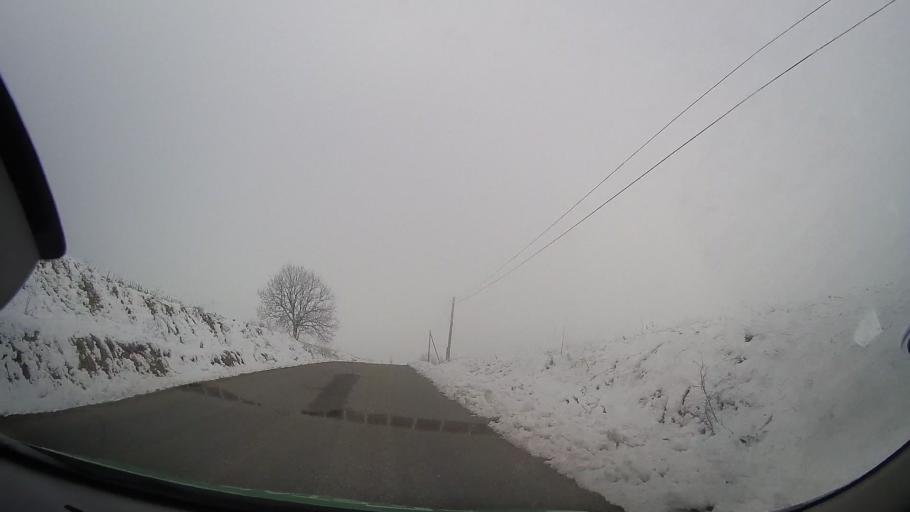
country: RO
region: Bacau
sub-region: Comuna Stanisesti
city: Stanisesti
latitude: 46.4107
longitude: 27.2705
